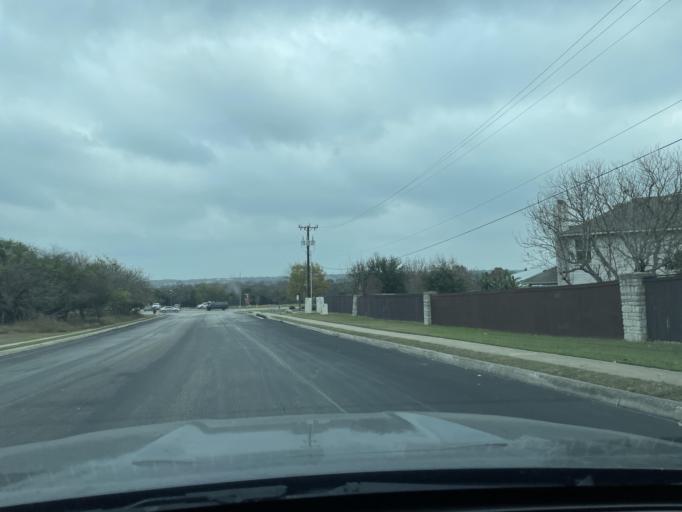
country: US
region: Texas
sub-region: Bexar County
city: Helotes
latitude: 29.5595
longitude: -98.6320
